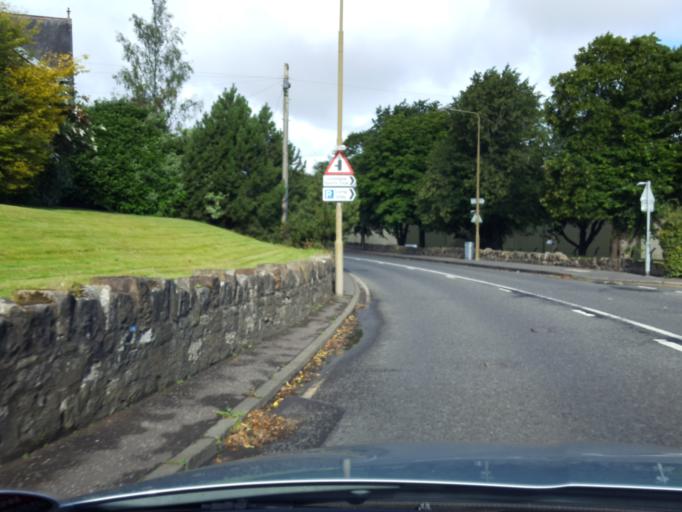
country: GB
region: Scotland
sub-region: West Lothian
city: Linlithgow
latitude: 55.9766
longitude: -3.5856
